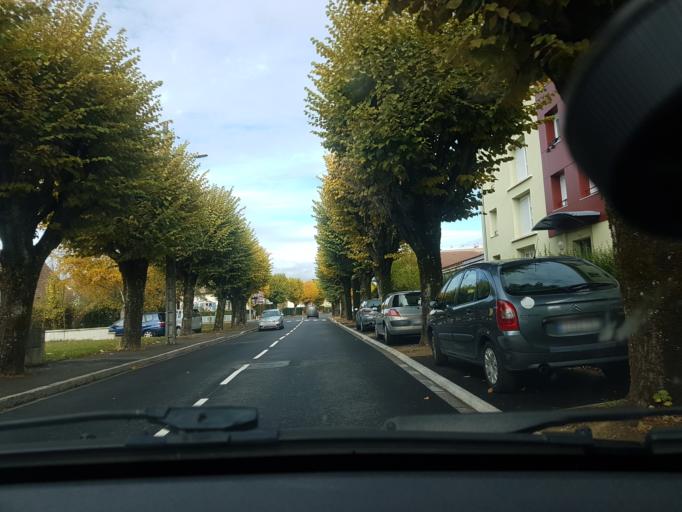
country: FR
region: Franche-Comte
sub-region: Territoire de Belfort
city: Danjoutin
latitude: 47.6227
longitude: 6.8519
